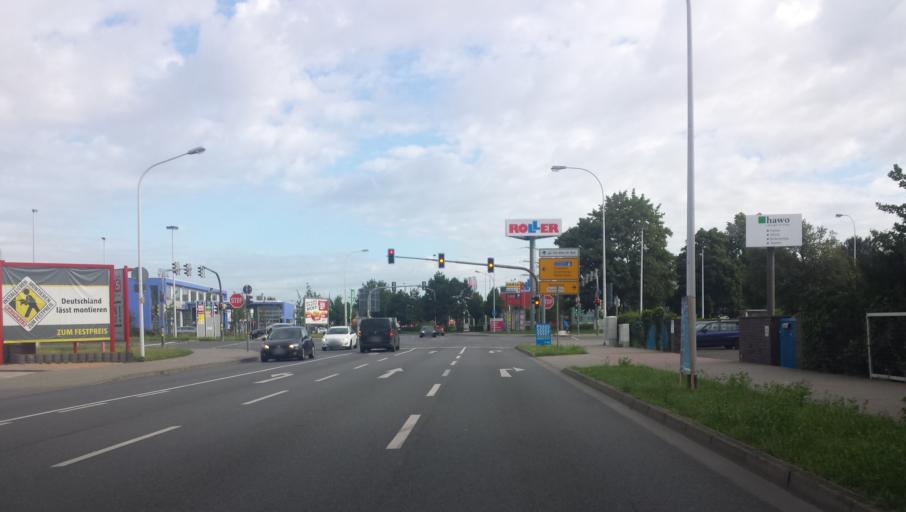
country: DE
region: Hesse
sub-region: Regierungsbezirk Darmstadt
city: Darmstadt
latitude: 49.8878
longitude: 8.6453
